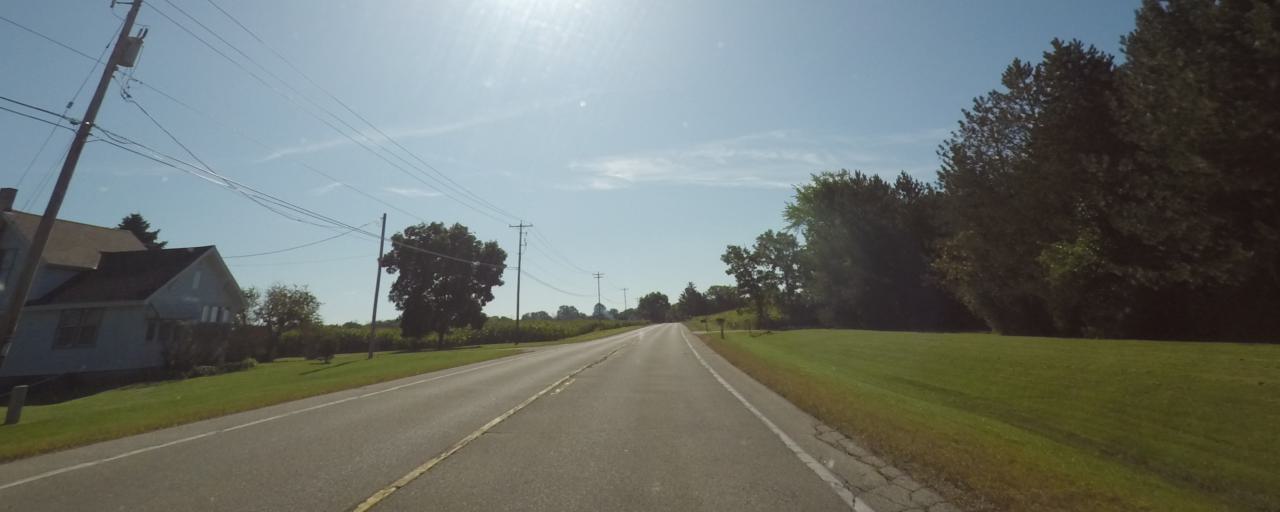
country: US
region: Wisconsin
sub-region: Waukesha County
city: Dousman
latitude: 43.0263
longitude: -88.5054
